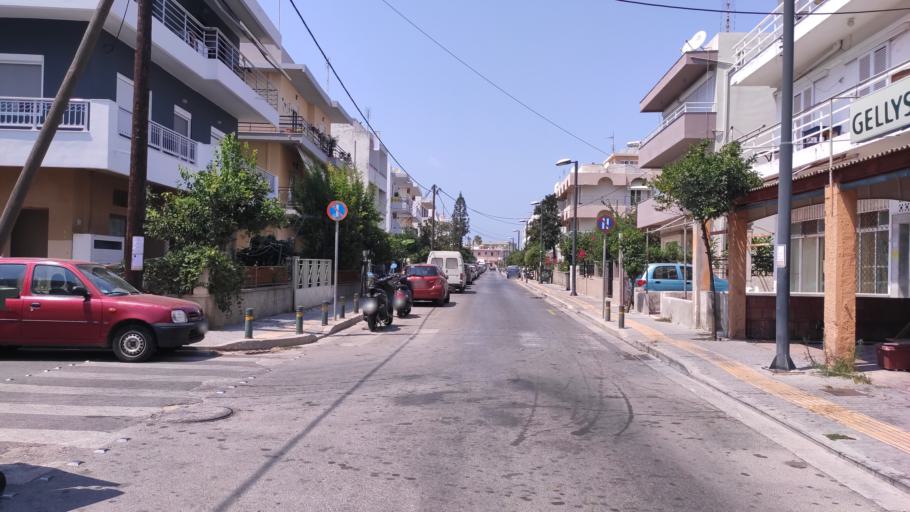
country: GR
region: South Aegean
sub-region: Nomos Dodekanisou
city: Kos
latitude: 36.8992
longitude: 27.2848
